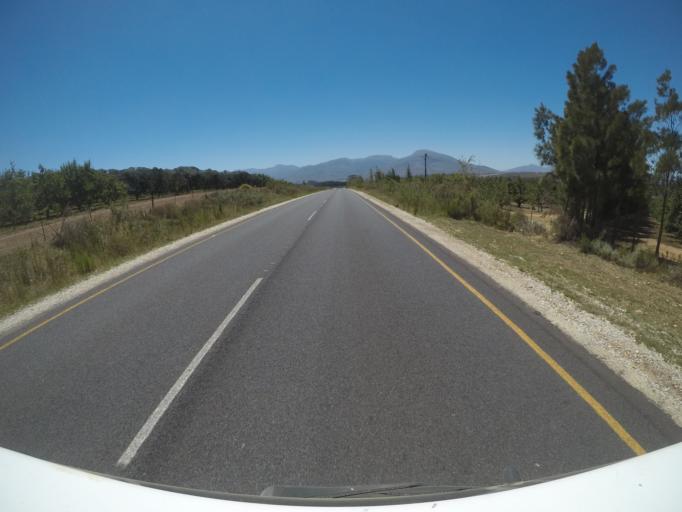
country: ZA
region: Western Cape
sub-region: Overberg District Municipality
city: Grabouw
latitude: -34.0640
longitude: 19.1340
